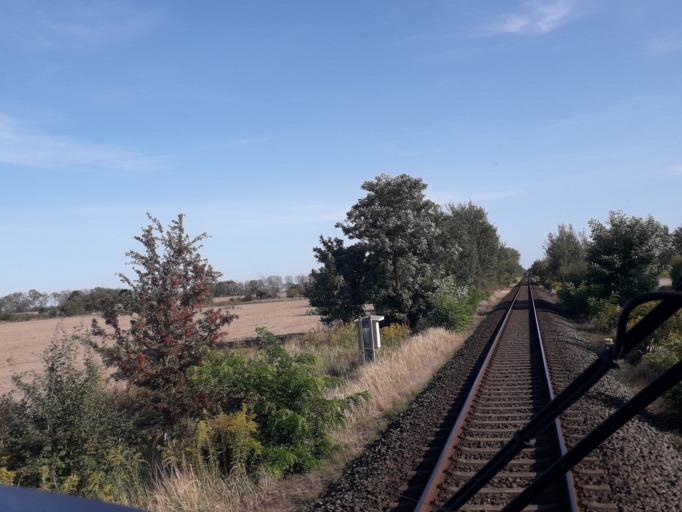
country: DE
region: Brandenburg
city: Velten
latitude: 52.7016
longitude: 13.1471
